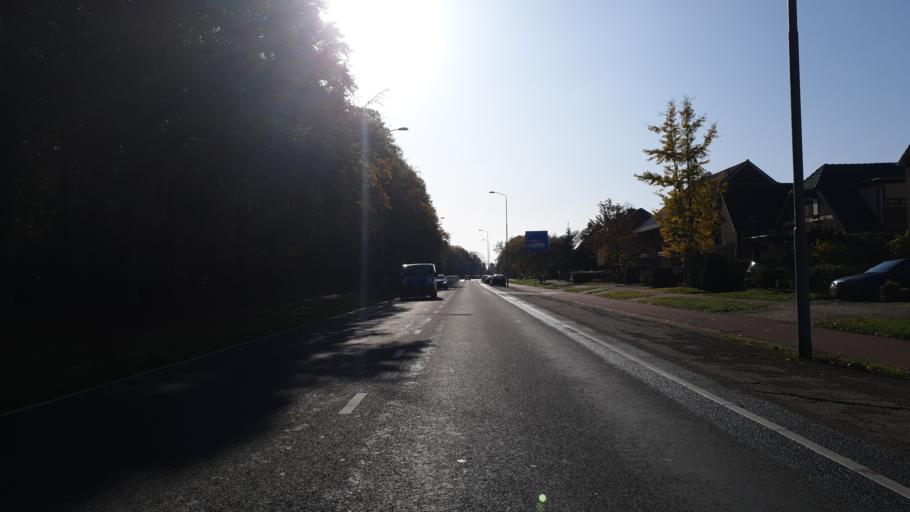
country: NL
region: Gelderland
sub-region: Gemeente Nijmegen
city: Nijmegen
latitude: 51.8112
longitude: 5.8537
